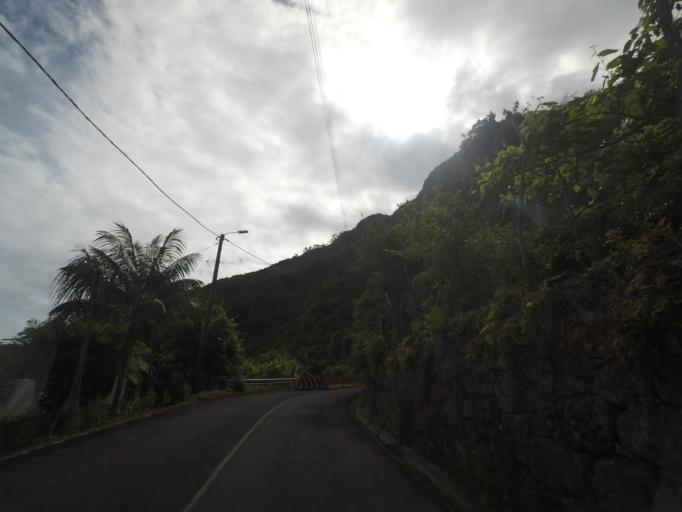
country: PT
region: Madeira
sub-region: Sao Vicente
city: Sao Vicente
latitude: 32.8202
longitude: -16.9904
